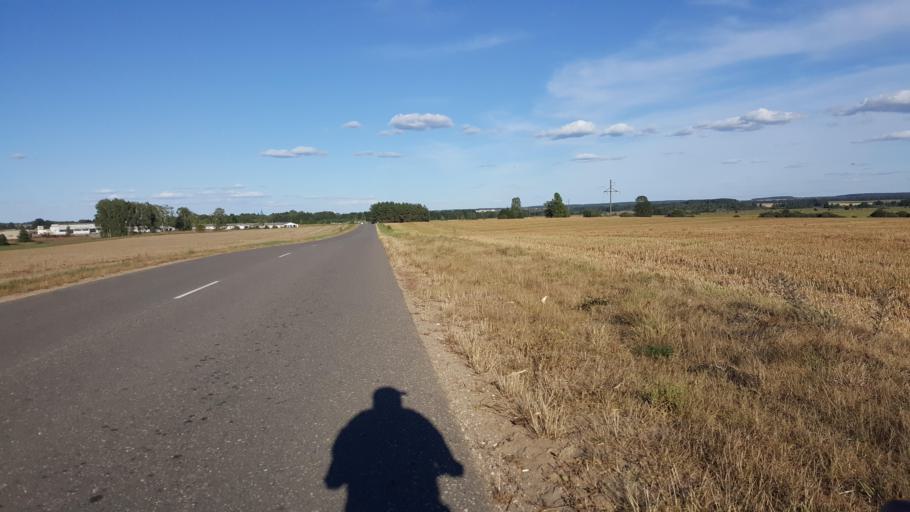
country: BY
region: Brest
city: Kamyanyets
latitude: 52.3897
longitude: 23.7440
